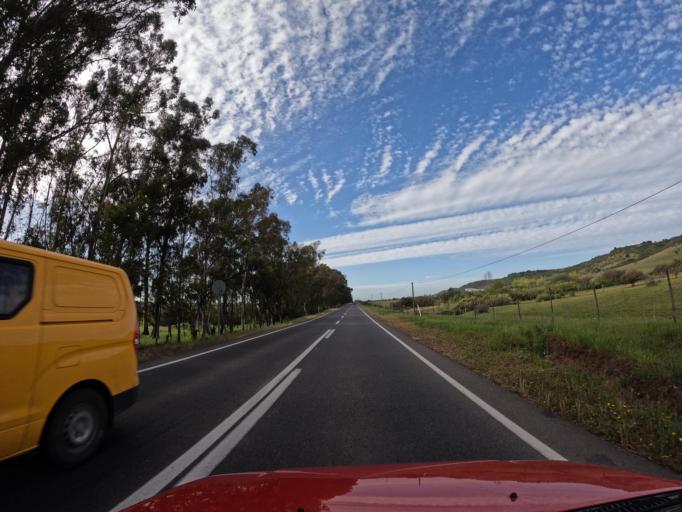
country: CL
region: O'Higgins
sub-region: Provincia de Colchagua
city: Santa Cruz
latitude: -34.1875
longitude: -71.7338
